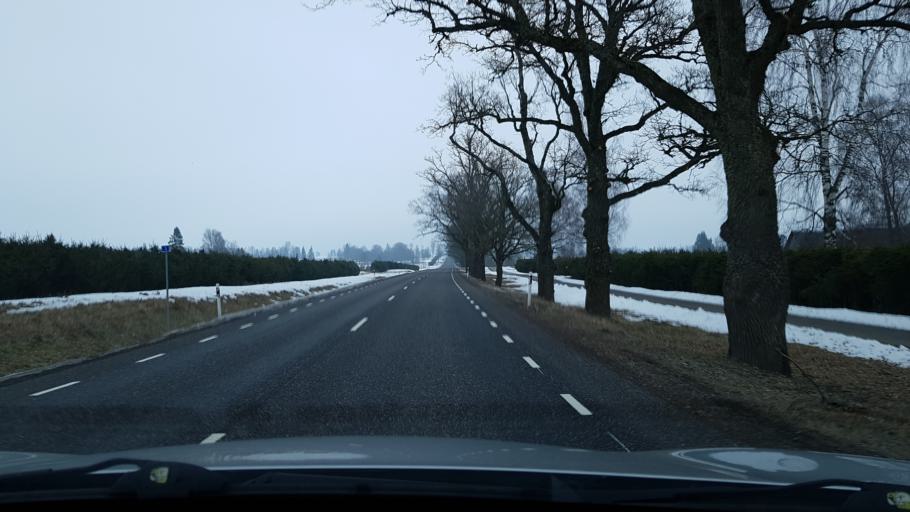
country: EE
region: Vorumaa
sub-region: Antsla vald
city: Vana-Antsla
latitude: 57.9089
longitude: 26.2945
